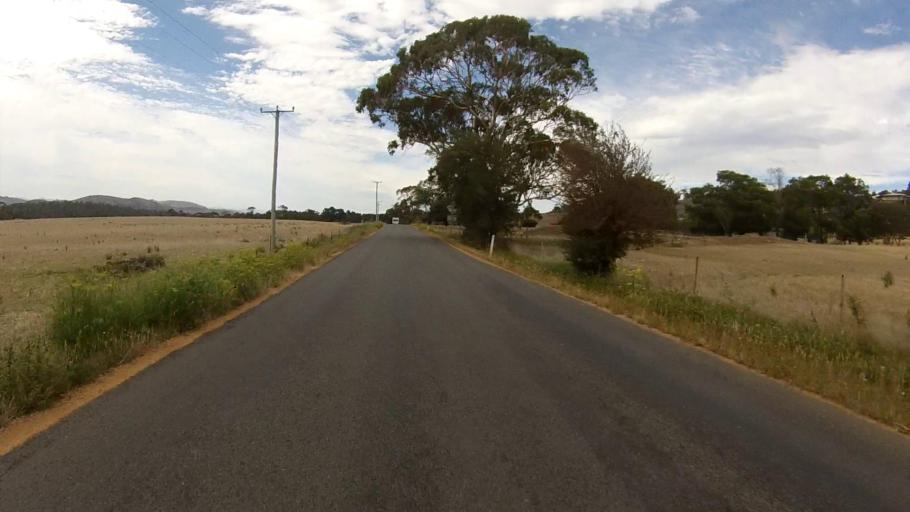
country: AU
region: Tasmania
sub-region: Brighton
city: Old Beach
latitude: -42.7394
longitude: 147.3544
